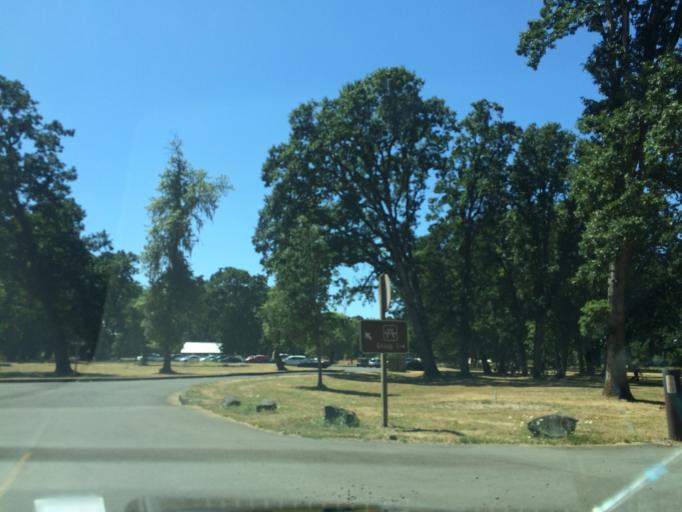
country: US
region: Oregon
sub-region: Yamhill County
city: Newberg
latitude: 45.2516
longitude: -122.8842
